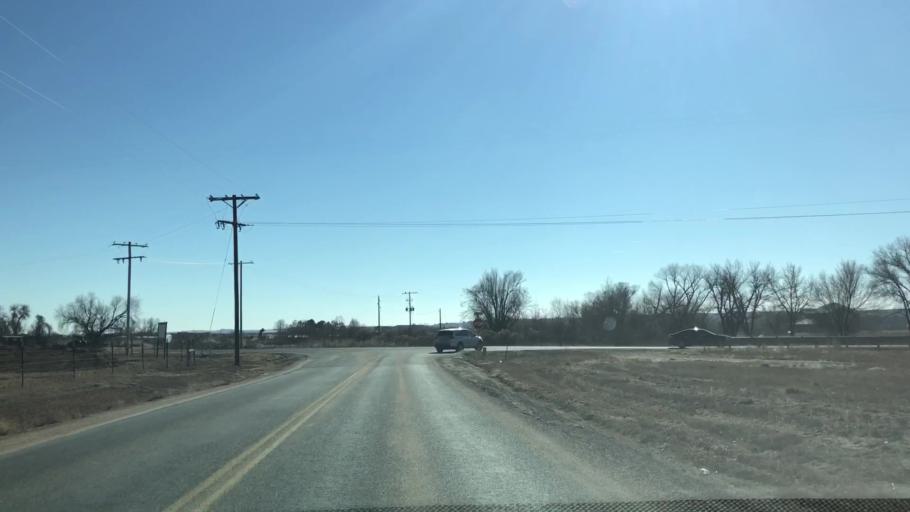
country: US
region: Colorado
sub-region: Weld County
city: Windsor
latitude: 40.4871
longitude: -104.9406
